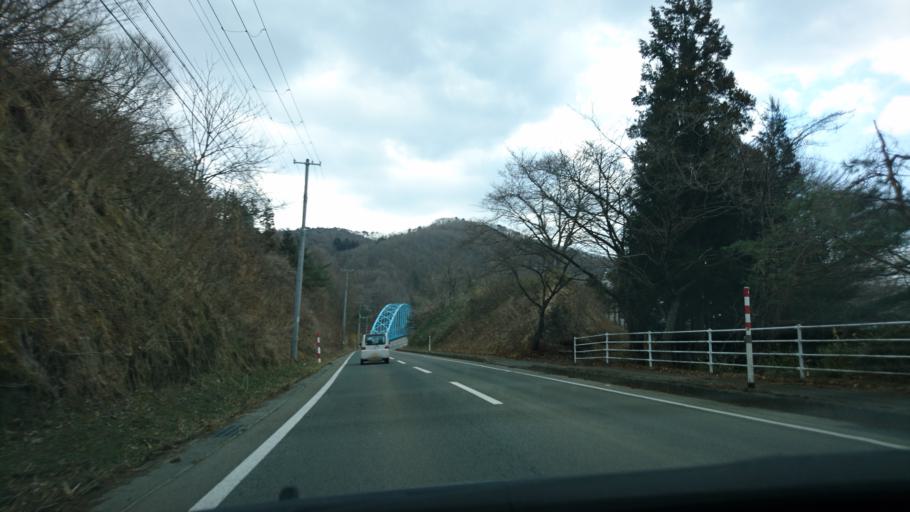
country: JP
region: Iwate
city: Shizukuishi
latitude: 39.6903
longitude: 141.0328
